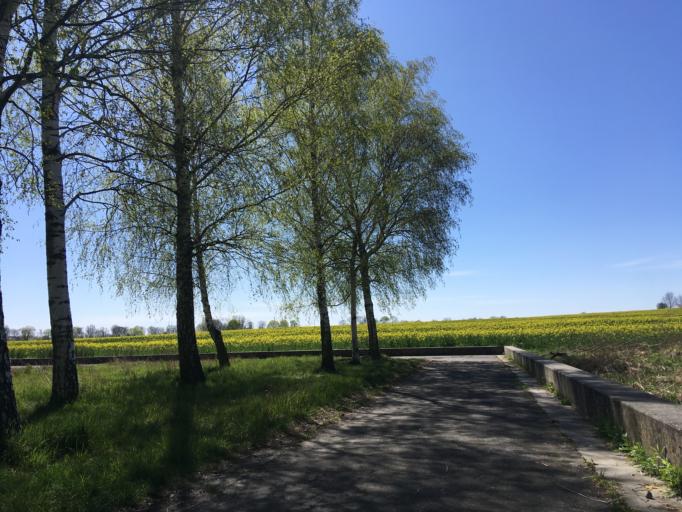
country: DE
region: Berlin
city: Karow
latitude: 52.6005
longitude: 13.4919
